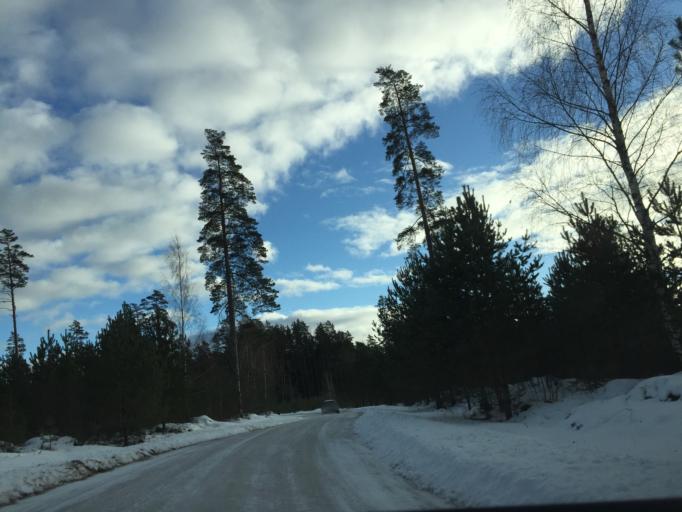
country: LV
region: Lielvarde
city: Lielvarde
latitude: 56.5674
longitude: 24.8274
